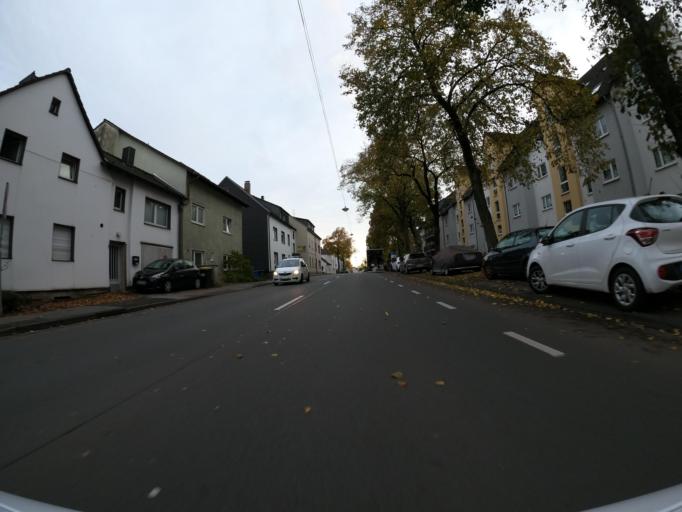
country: DE
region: North Rhine-Westphalia
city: Haan
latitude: 51.1982
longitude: 7.0160
